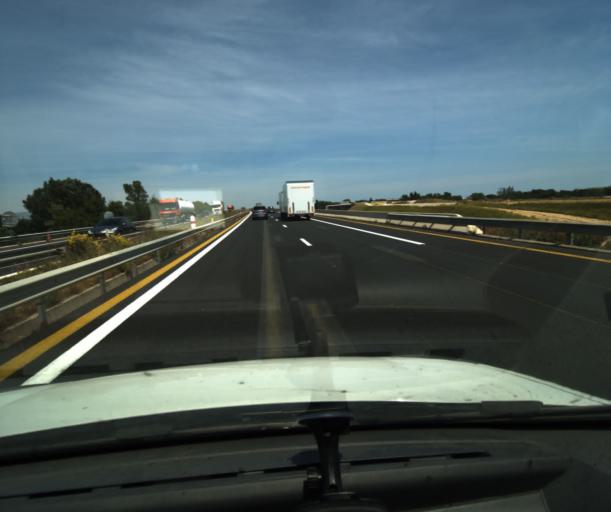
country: FR
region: Languedoc-Roussillon
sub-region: Departement des Pyrenees-Orientales
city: Saint-Esteve
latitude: 42.7111
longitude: 2.8697
